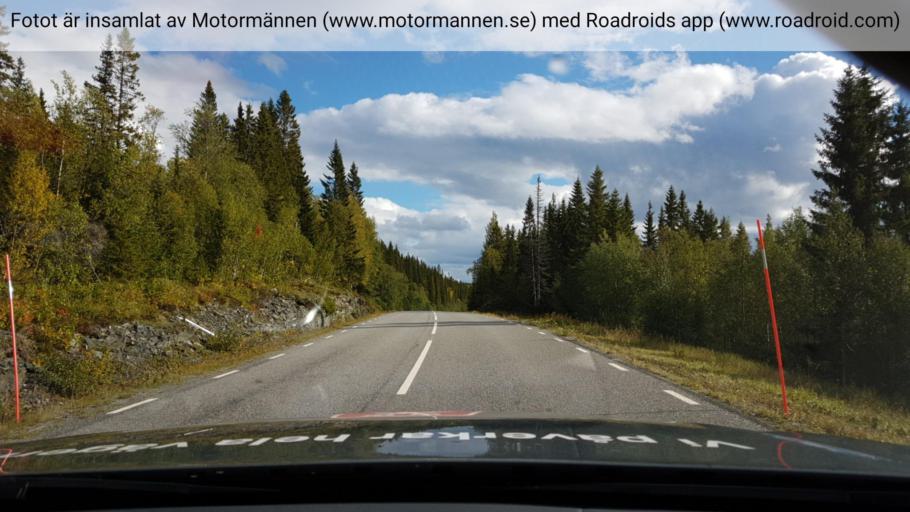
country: SE
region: Jaemtland
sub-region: Are Kommun
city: Are
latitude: 63.5093
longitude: 13.1418
